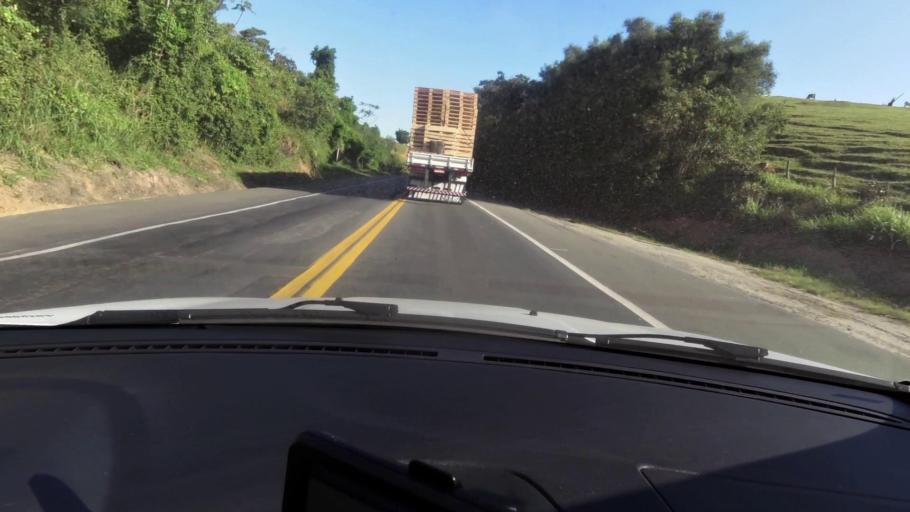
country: BR
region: Espirito Santo
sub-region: Alfredo Chaves
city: Alfredo Chaves
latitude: -20.6678
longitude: -40.6630
